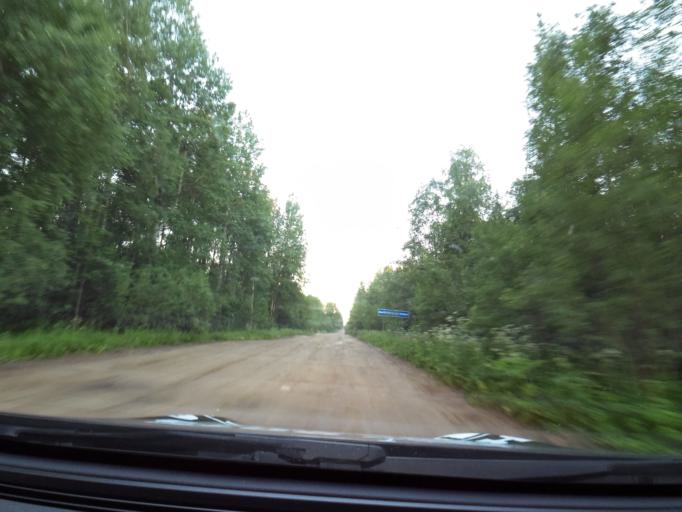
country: RU
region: Leningrad
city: Voznesen'ye
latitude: 60.8908
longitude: 35.5142
